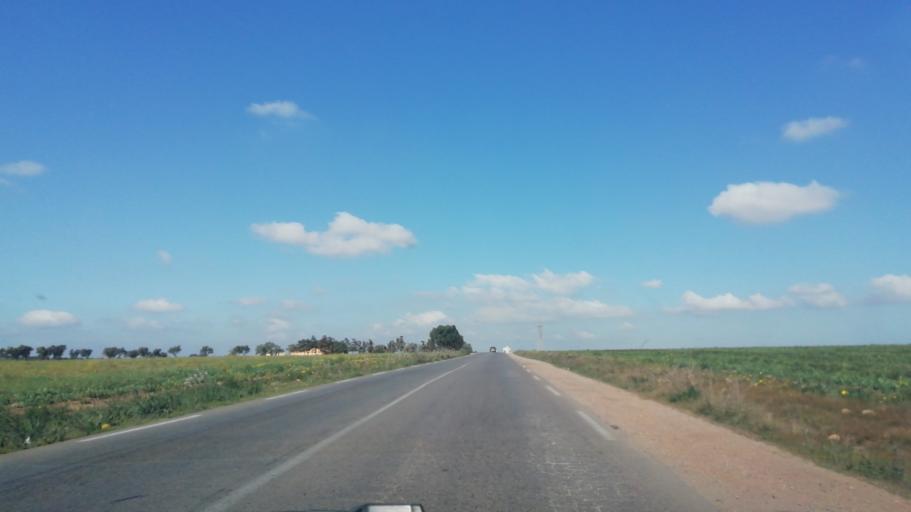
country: DZ
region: Oran
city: Ain el Bya
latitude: 35.7150
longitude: -0.2322
